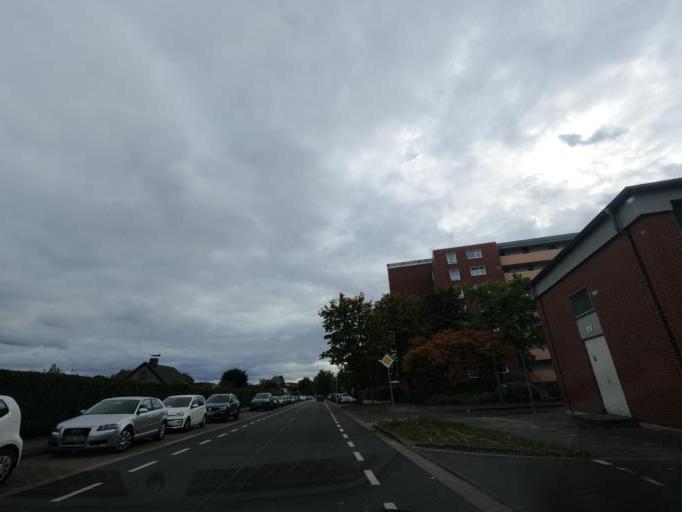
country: DE
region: Lower Saxony
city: Braunschweig
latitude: 52.2482
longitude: 10.4805
